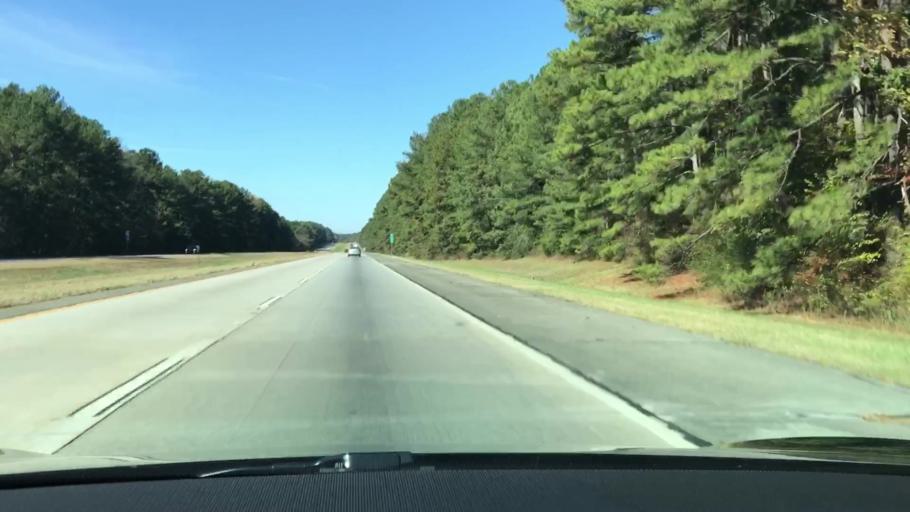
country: US
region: Georgia
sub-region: Greene County
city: Union Point
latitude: 33.5416
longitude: -83.0133
